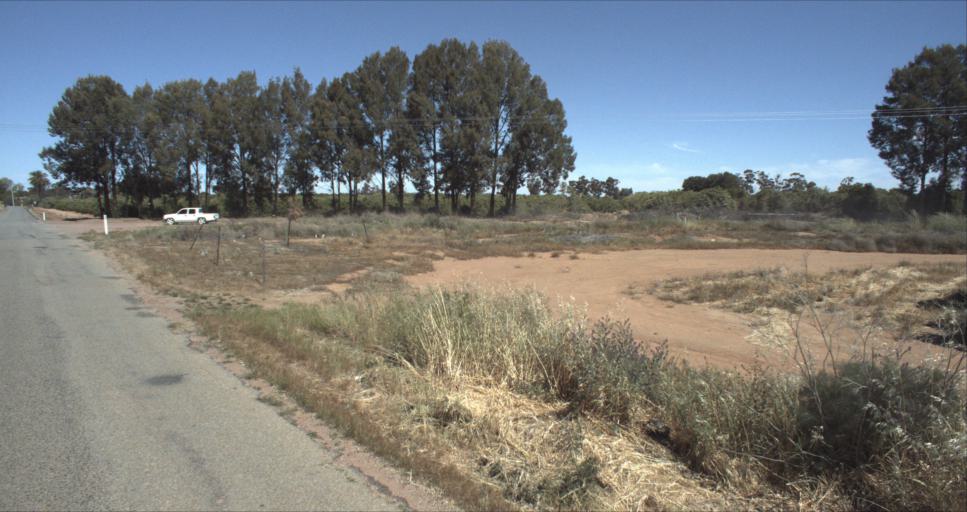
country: AU
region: New South Wales
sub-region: Leeton
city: Leeton
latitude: -34.5465
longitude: 146.3690
